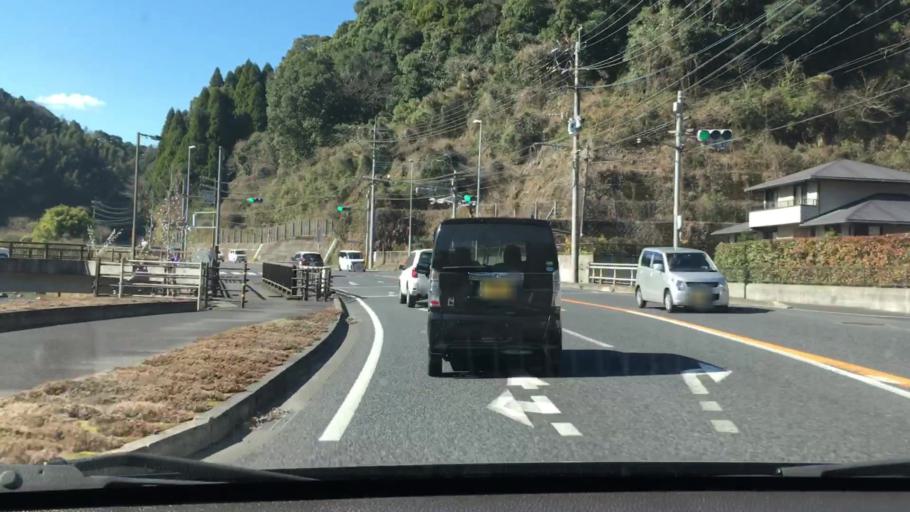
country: JP
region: Kagoshima
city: Kagoshima-shi
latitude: 31.6522
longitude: 130.5115
